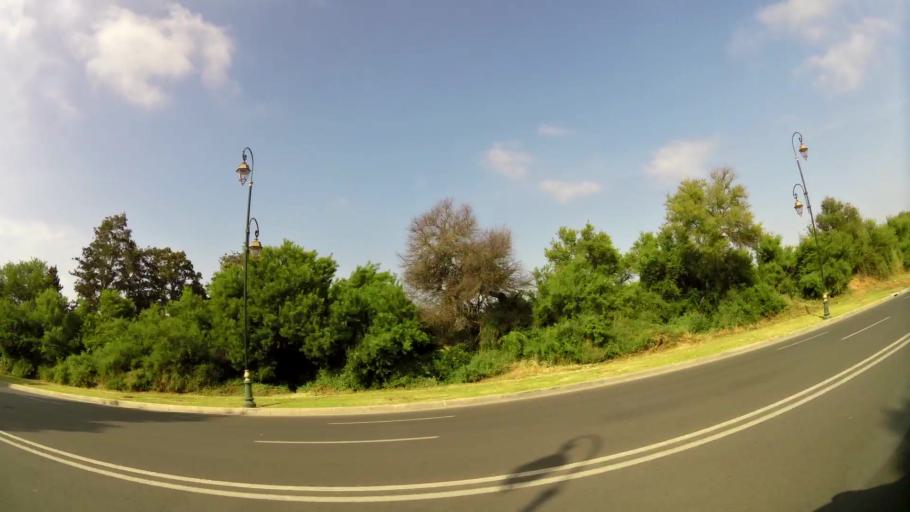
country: MA
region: Rabat-Sale-Zemmour-Zaer
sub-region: Rabat
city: Rabat
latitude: 33.9531
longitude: -6.8149
